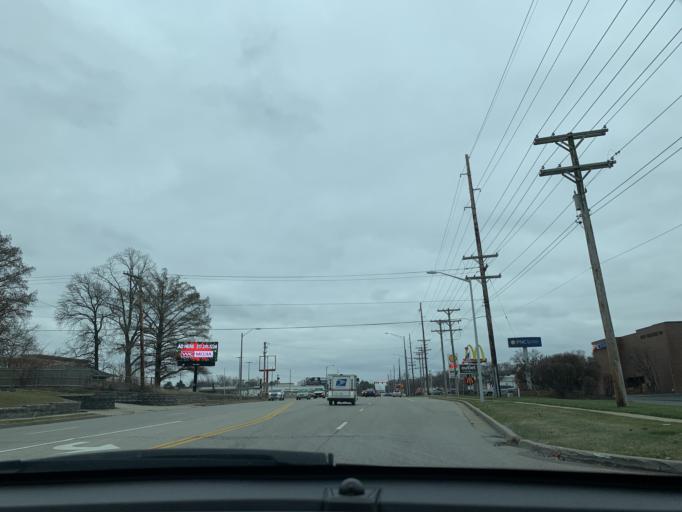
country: US
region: Illinois
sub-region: Sangamon County
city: Jerome
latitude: 39.7663
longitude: -89.6870
